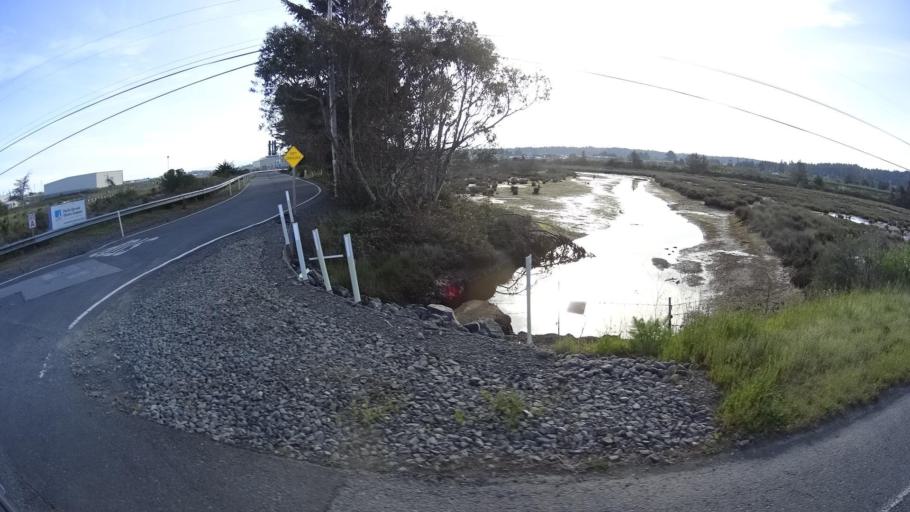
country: US
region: California
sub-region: Humboldt County
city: Humboldt Hill
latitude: 40.7385
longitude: -124.2127
